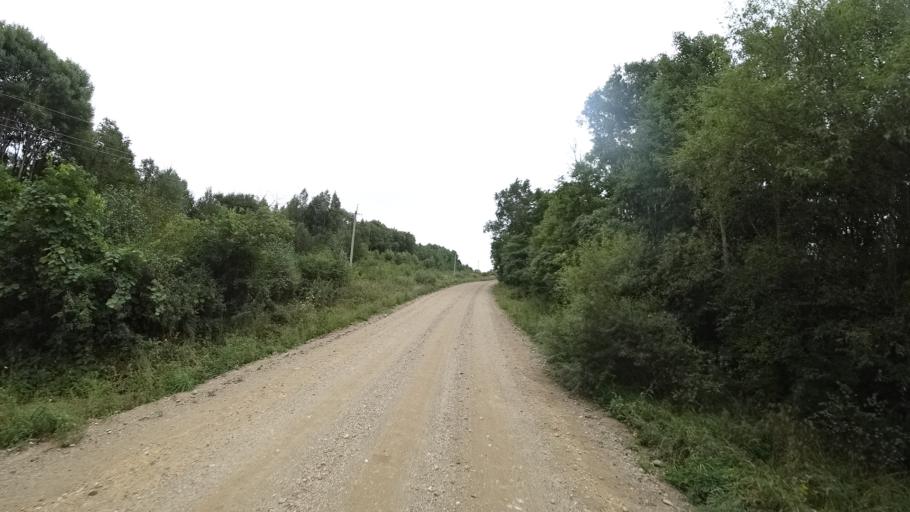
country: RU
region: Primorskiy
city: Lyalichi
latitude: 44.0646
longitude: 132.4782
